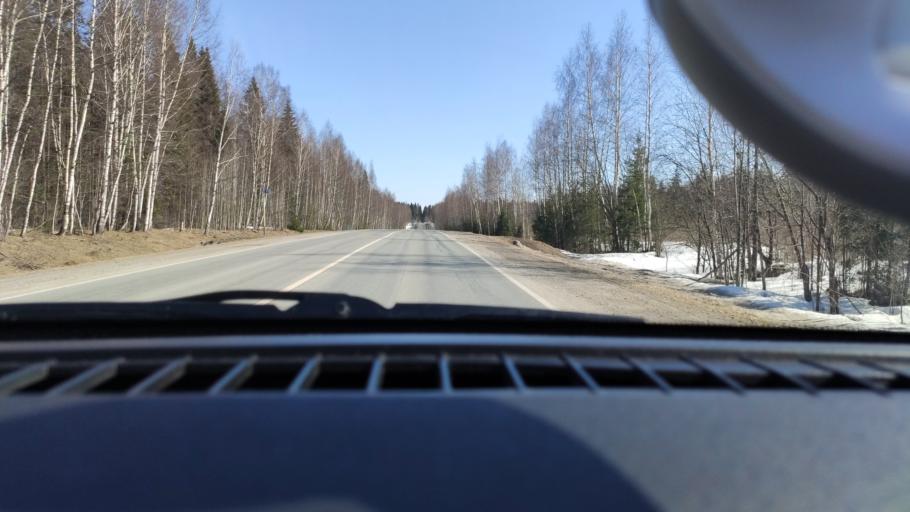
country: RU
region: Perm
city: Perm
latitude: 58.1368
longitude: 56.2874
